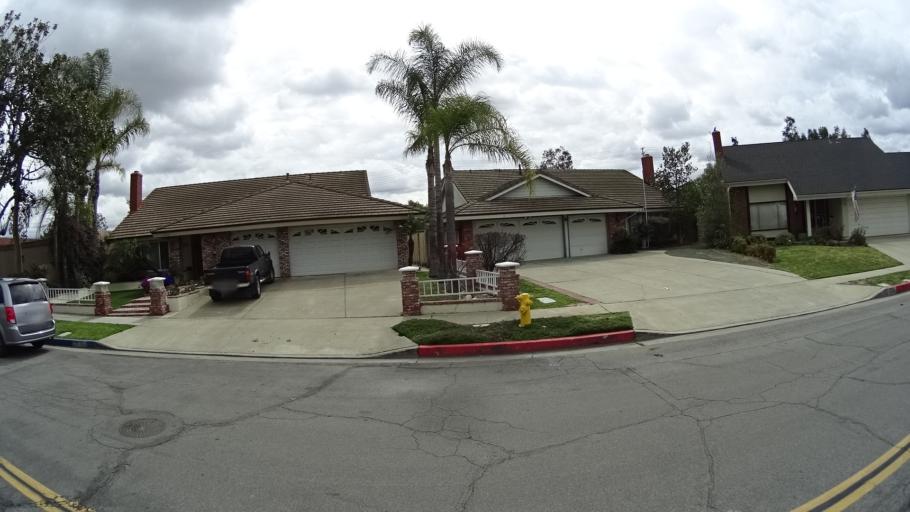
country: US
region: California
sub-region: Orange County
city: Placentia
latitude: 33.8387
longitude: -117.8740
